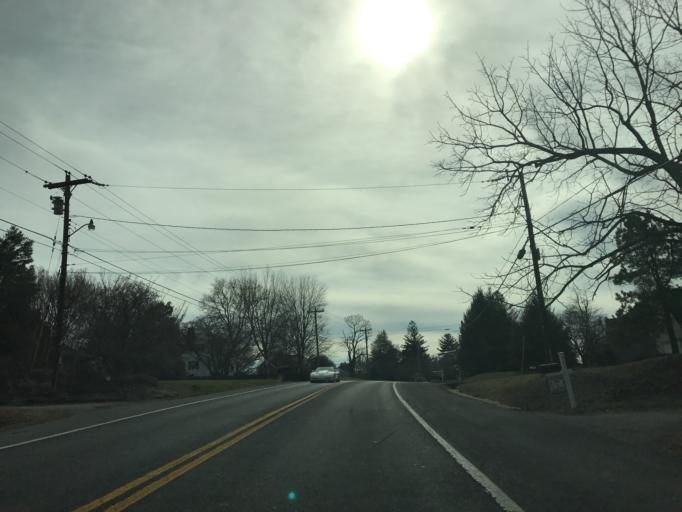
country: US
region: Maryland
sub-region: Queen Anne's County
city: Centreville
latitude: 39.0526
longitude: -76.0553
